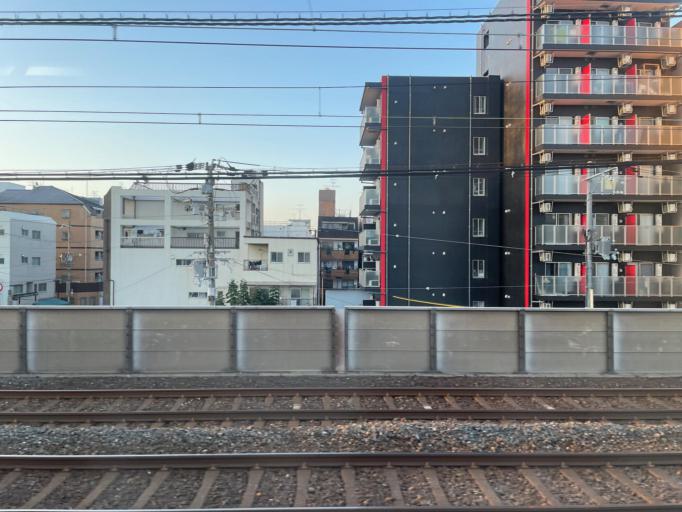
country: JP
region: Osaka
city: Osaka-shi
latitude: 34.6650
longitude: 135.5467
